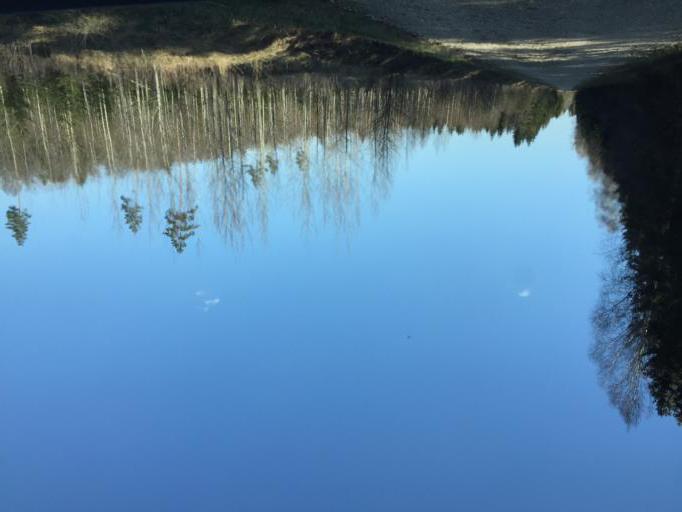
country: LV
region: Kegums
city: Kegums
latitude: 56.8749
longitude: 24.8002
